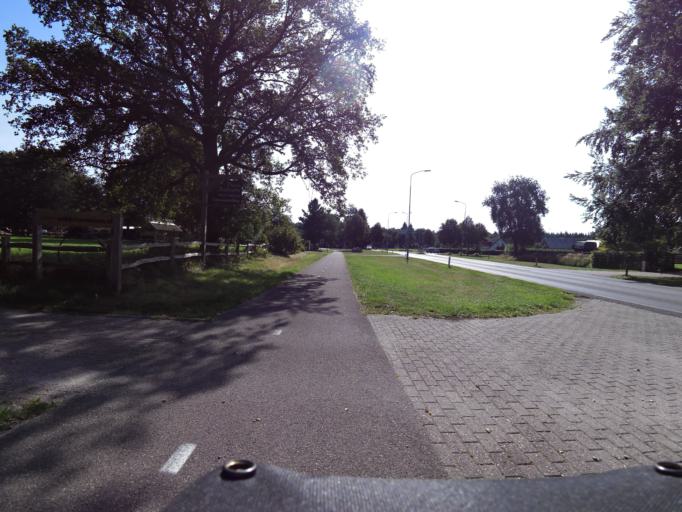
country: NL
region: Gelderland
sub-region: Gemeente Apeldoorn
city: Uddel
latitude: 52.2221
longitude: 5.7787
